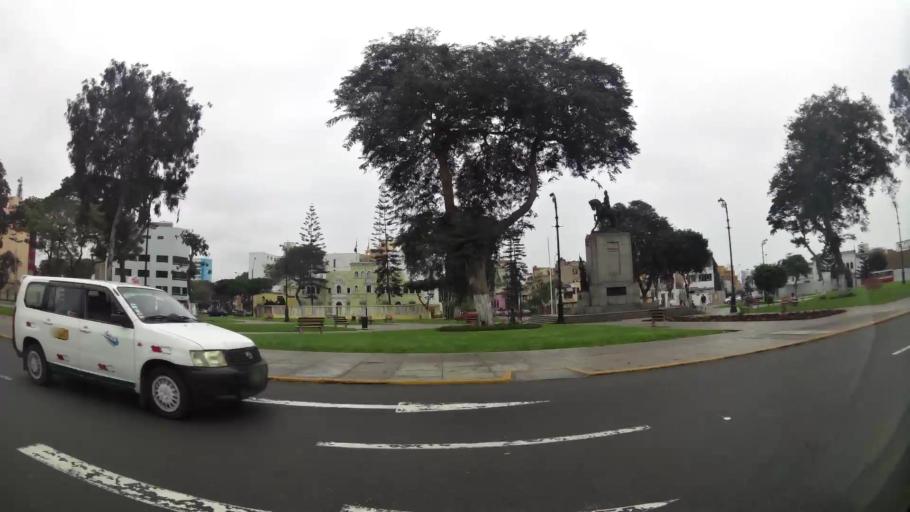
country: PE
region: Lima
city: Lima
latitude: -12.0748
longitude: -77.0433
